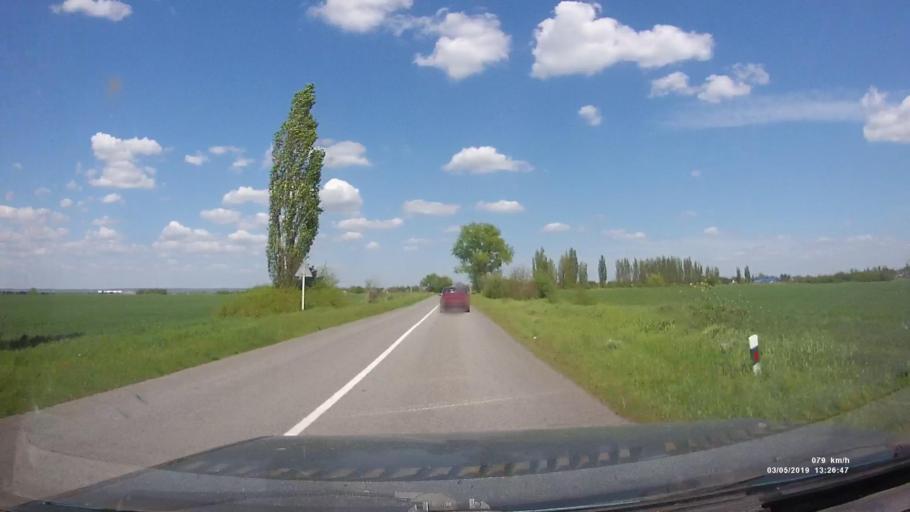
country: RU
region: Rostov
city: Semikarakorsk
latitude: 47.5736
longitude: 40.8254
